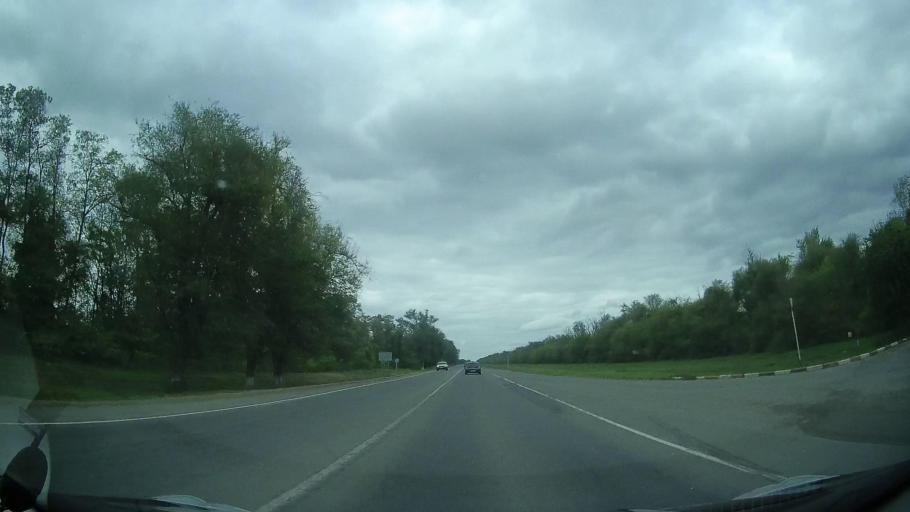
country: RU
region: Rostov
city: Yegorlykskaya
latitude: 46.5917
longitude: 40.6276
